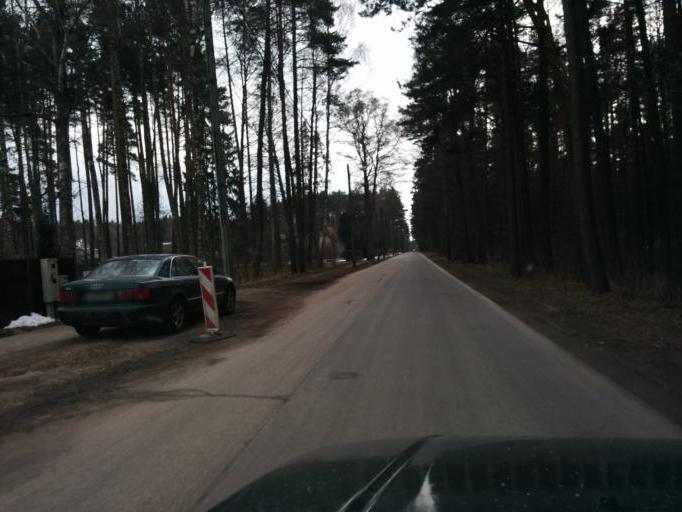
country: LV
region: Jurmala
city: Jurmala
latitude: 56.9506
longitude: 23.7252
